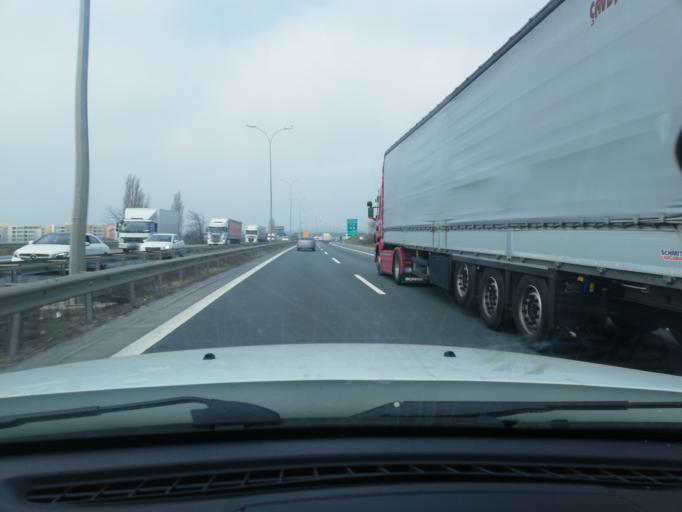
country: TR
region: Istanbul
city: Selimpasa
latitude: 41.0752
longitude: 28.3766
